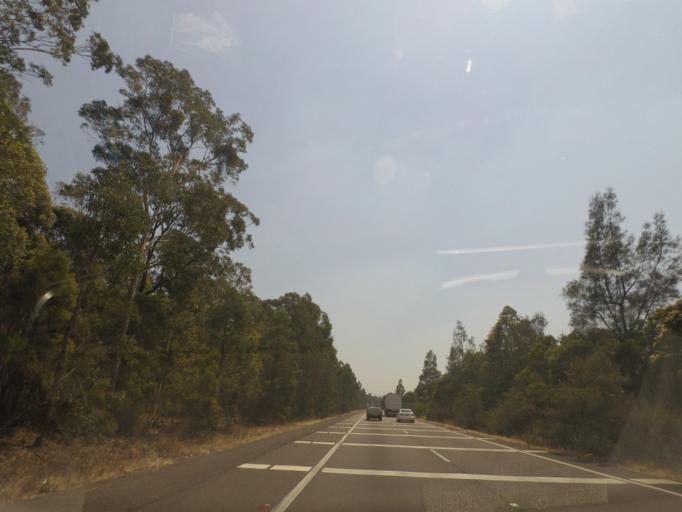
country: AU
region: New South Wales
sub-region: Newcastle
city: Beresfield
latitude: -32.8238
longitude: 151.6335
